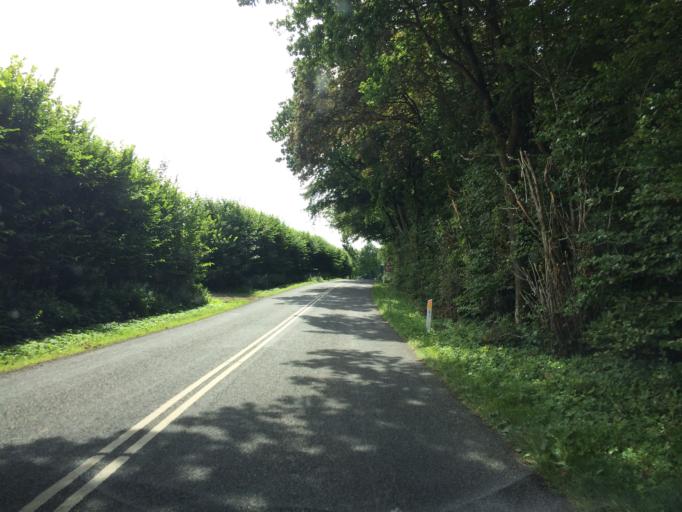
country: DK
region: South Denmark
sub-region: Faaborg-Midtfyn Kommune
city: Faaborg
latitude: 55.1587
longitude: 10.2623
